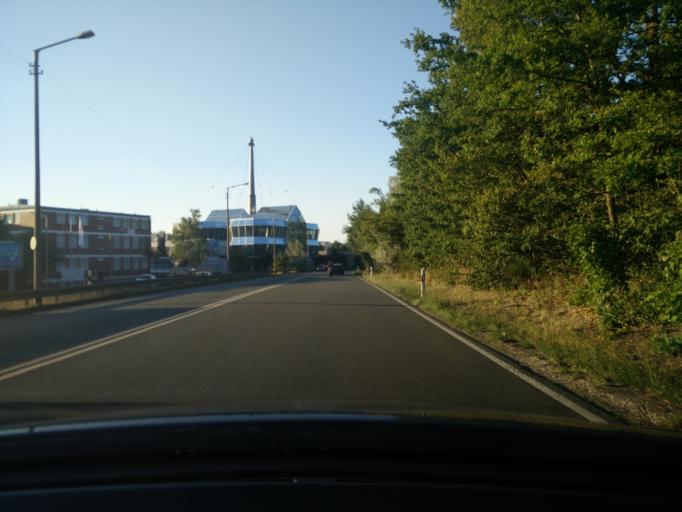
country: DE
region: Bavaria
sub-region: Regierungsbezirk Mittelfranken
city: Wendelstein
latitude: 49.4017
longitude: 11.1279
